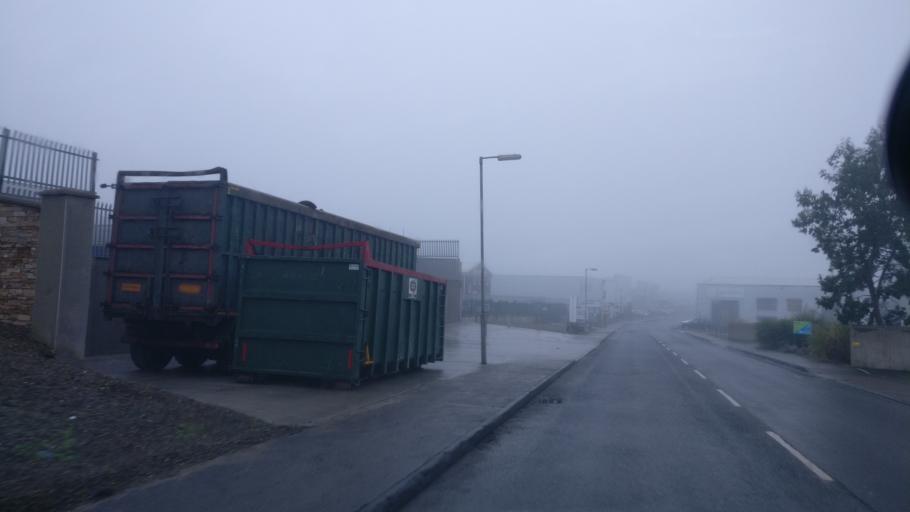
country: IE
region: Munster
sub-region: County Limerick
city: Luimneach
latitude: 52.6481
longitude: -8.5877
